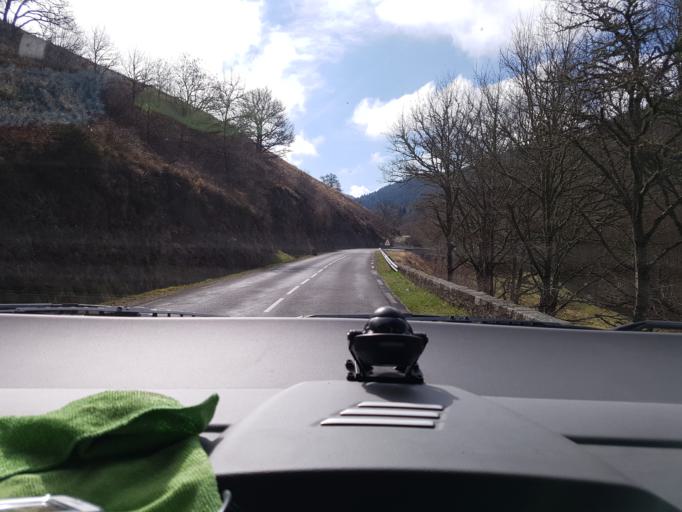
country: FR
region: Auvergne
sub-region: Departement du Cantal
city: Chaudes-Aigues
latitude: 44.8793
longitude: 2.9979
